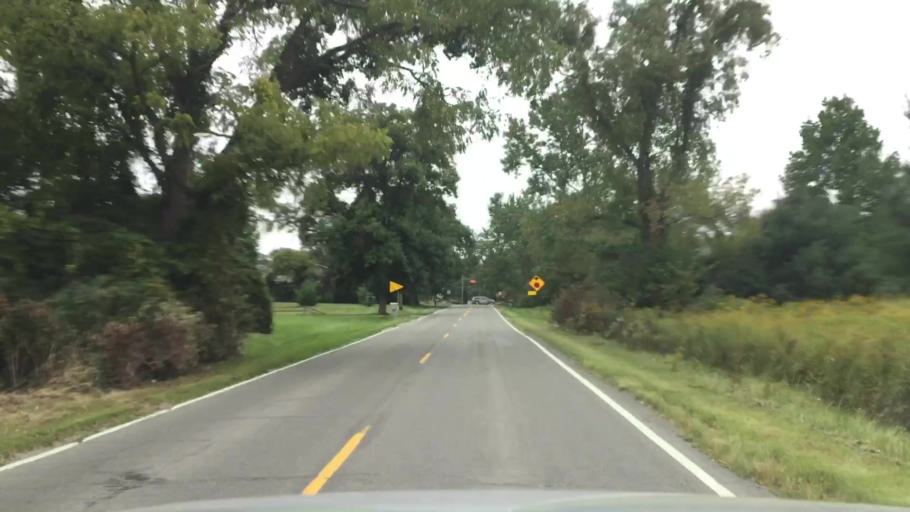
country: US
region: Michigan
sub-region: Washtenaw County
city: Milan
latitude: 42.1542
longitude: -83.6531
